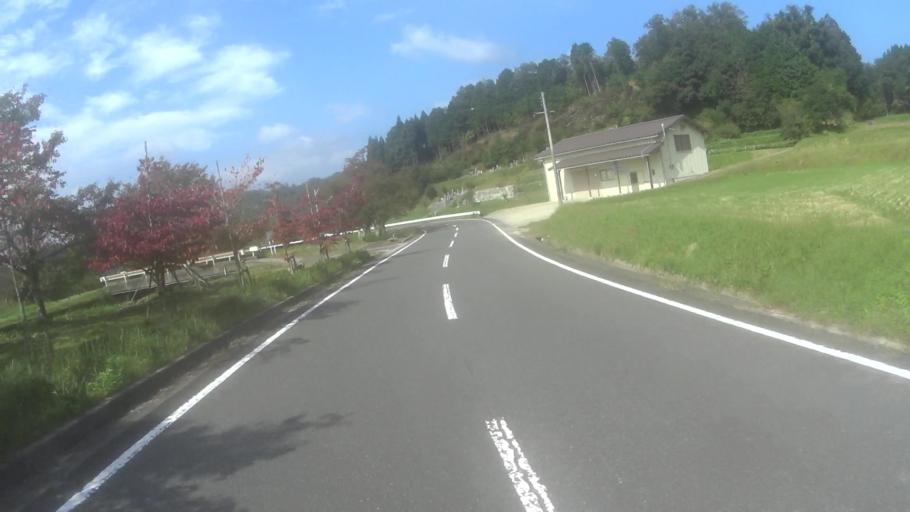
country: JP
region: Kyoto
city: Miyazu
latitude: 35.5988
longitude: 135.1423
